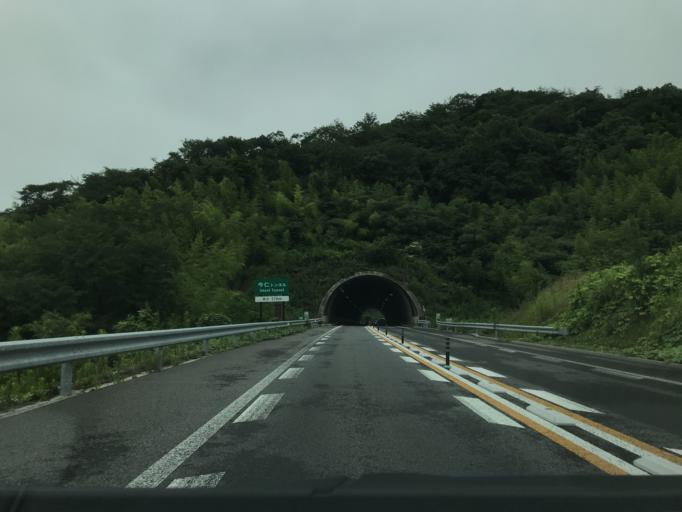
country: JP
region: Fukuoka
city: Nakatsu
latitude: 33.5186
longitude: 131.2656
